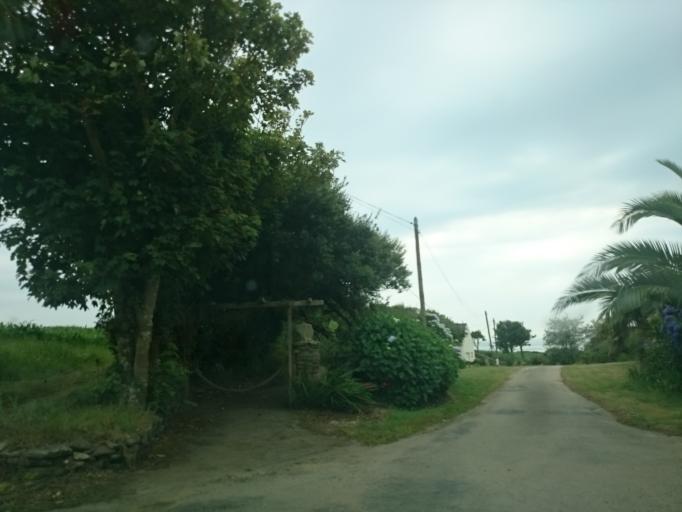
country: FR
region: Brittany
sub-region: Departement du Finistere
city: Le Conquet
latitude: 48.3975
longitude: -4.7695
